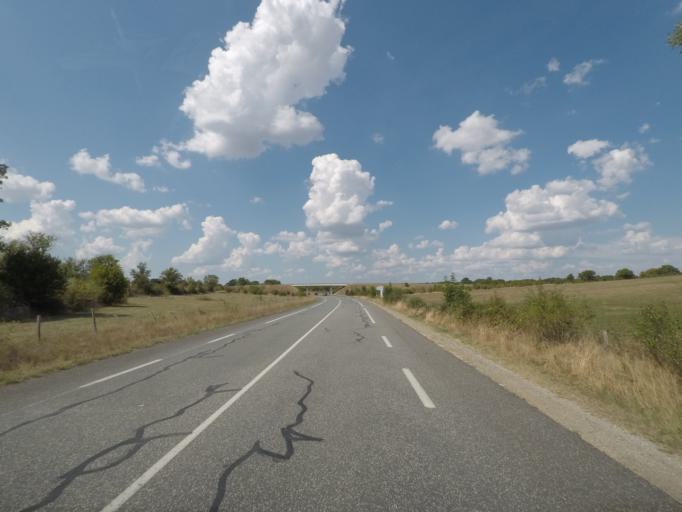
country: FR
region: Midi-Pyrenees
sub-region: Departement du Lot
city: Gramat
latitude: 44.6889
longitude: 1.6002
